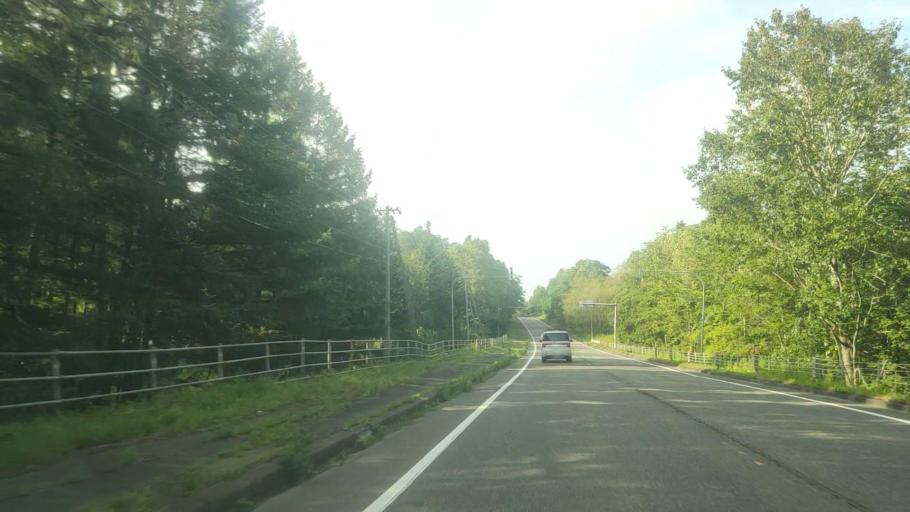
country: JP
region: Hokkaido
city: Chitose
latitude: 42.8676
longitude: 141.8226
